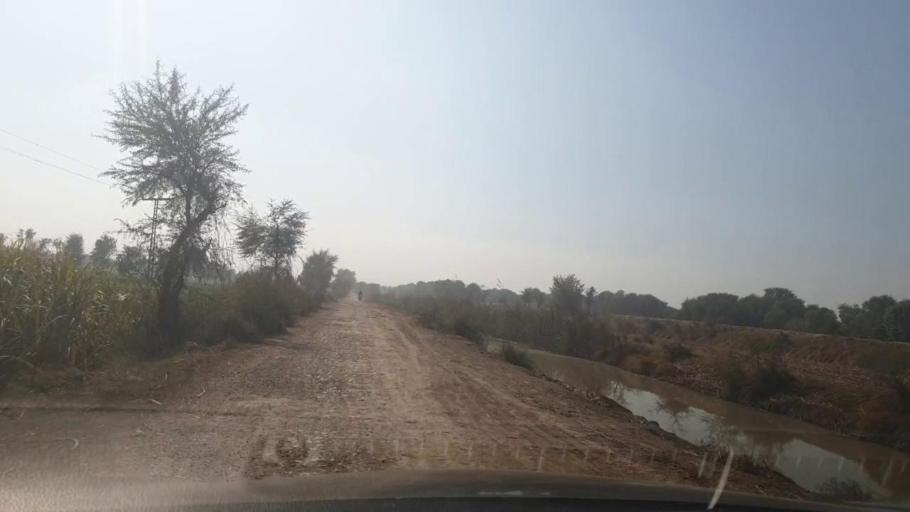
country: PK
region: Sindh
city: Ubauro
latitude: 28.1430
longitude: 69.6871
